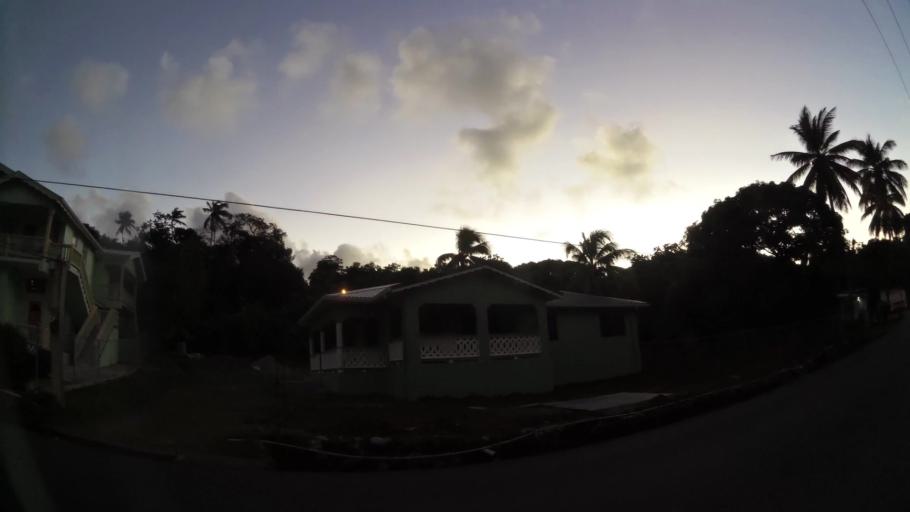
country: LC
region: Castries Quarter
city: Bisee
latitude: 14.0376
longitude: -60.9516
